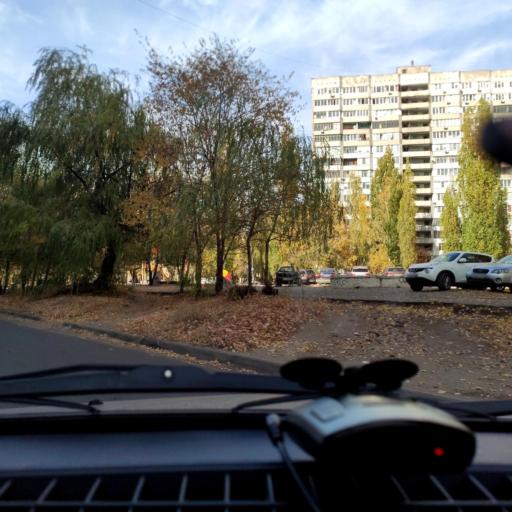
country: RU
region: Voronezj
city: Podgornoye
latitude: 51.7030
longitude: 39.1540
